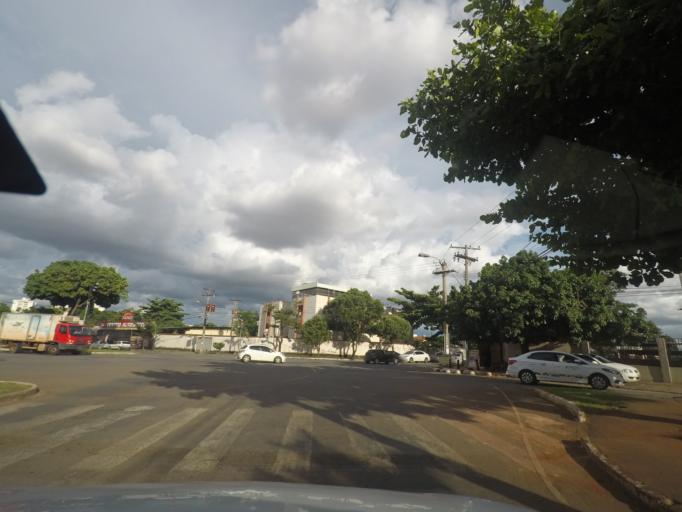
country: BR
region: Goias
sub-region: Goiania
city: Goiania
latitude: -16.6913
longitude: -49.3028
